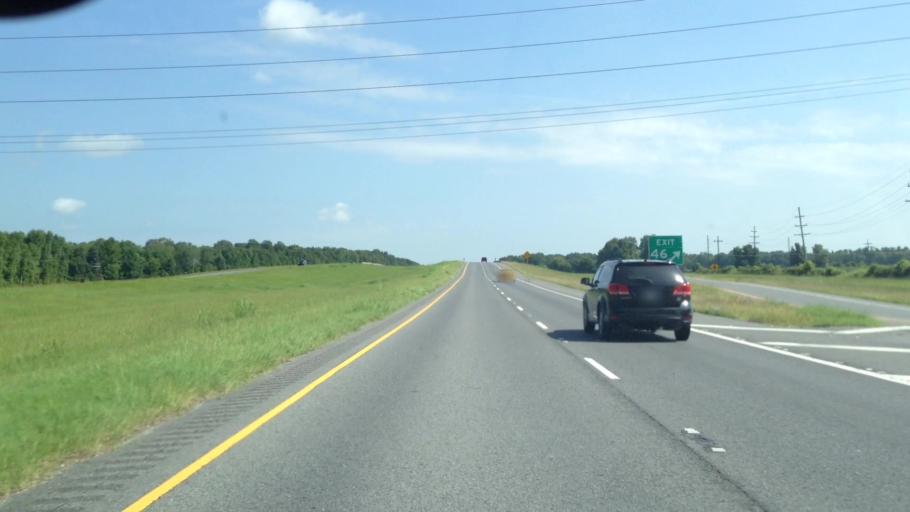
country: US
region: Louisiana
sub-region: Avoyelles Parish
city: Bunkie
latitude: 30.8618
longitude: -92.2279
